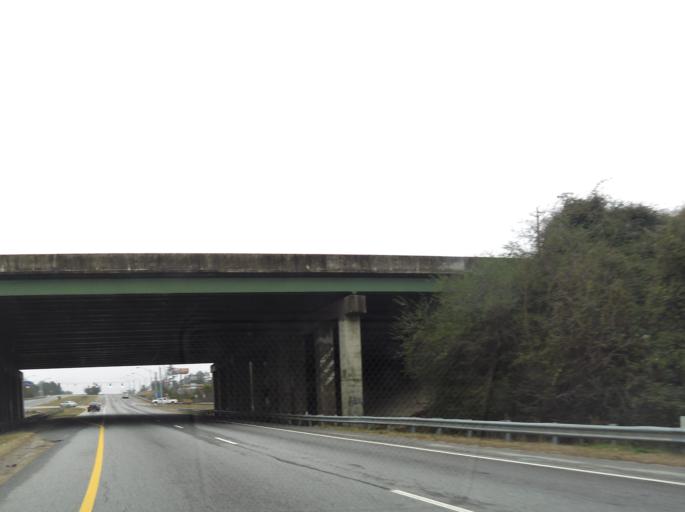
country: US
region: Georgia
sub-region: Bibb County
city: West Point
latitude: 32.8100
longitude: -83.7251
